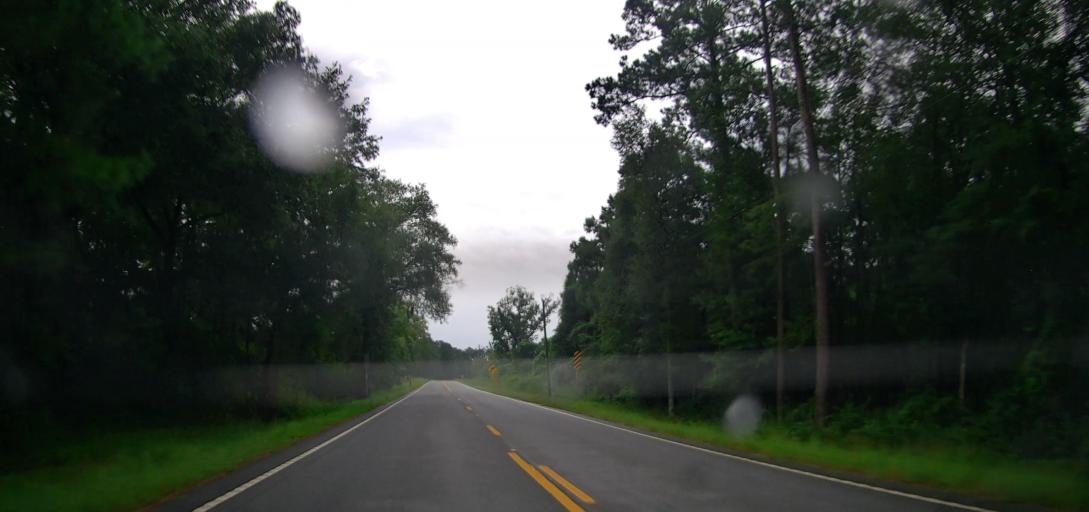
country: US
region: Georgia
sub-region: Ware County
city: Deenwood
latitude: 31.2787
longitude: -82.4227
